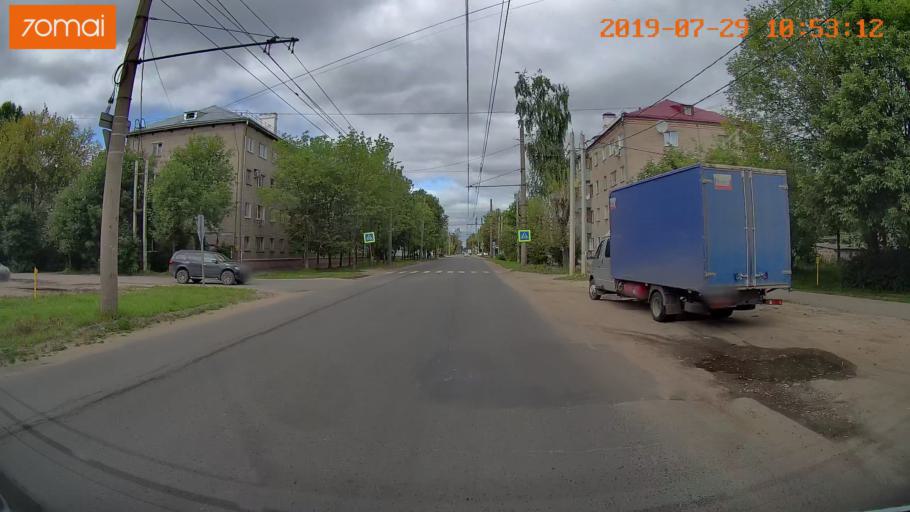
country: RU
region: Ivanovo
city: Kokhma
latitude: 56.9738
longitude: 41.0526
